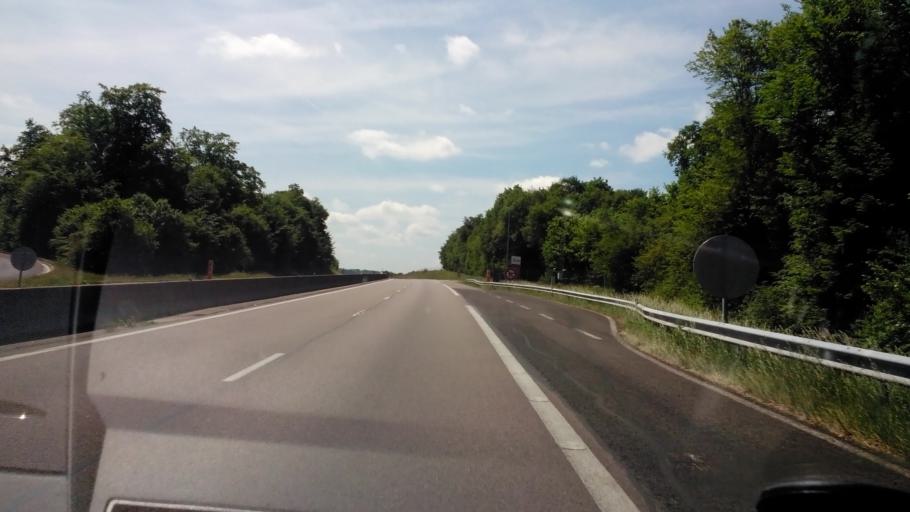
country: FR
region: Lorraine
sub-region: Departement de Meurthe-et-Moselle
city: Colombey-les-Belles
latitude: 48.4267
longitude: 5.8598
